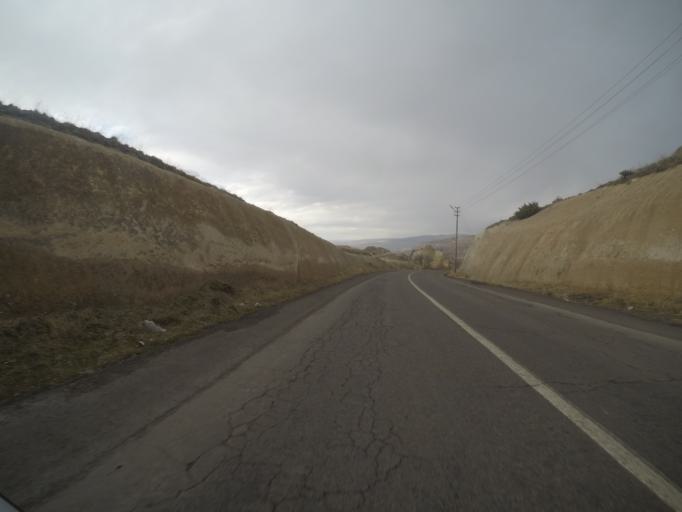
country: TR
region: Nevsehir
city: Goereme
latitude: 38.6329
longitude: 34.8568
